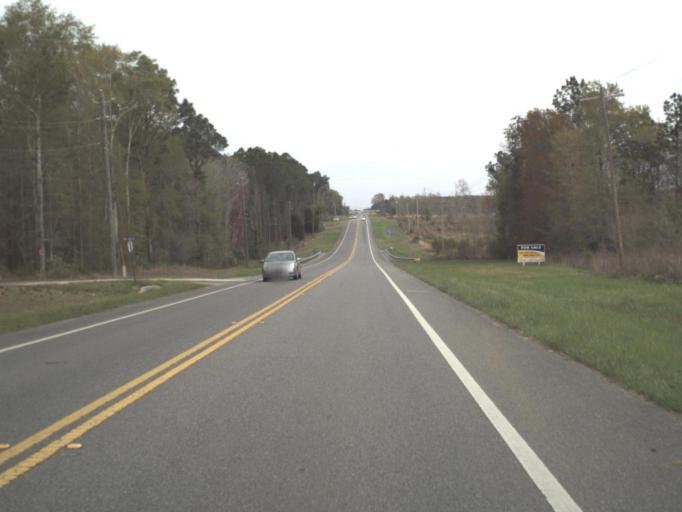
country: US
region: Florida
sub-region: Holmes County
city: Bonifay
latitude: 30.7476
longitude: -85.6850
